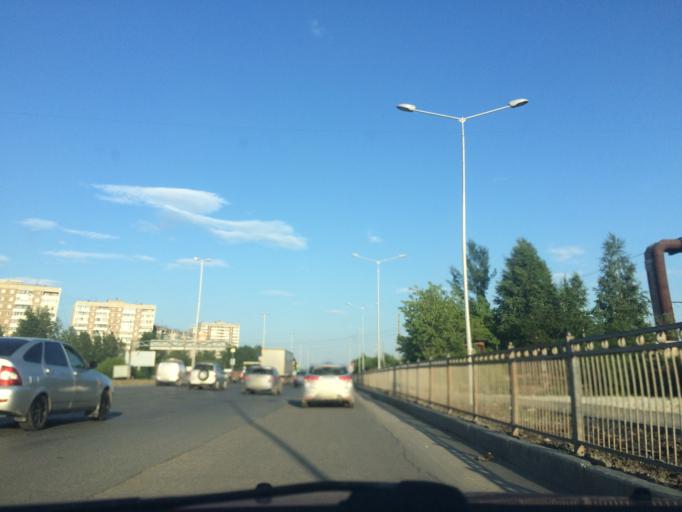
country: RU
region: Sverdlovsk
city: Yekaterinburg
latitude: 56.8285
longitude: 60.6790
